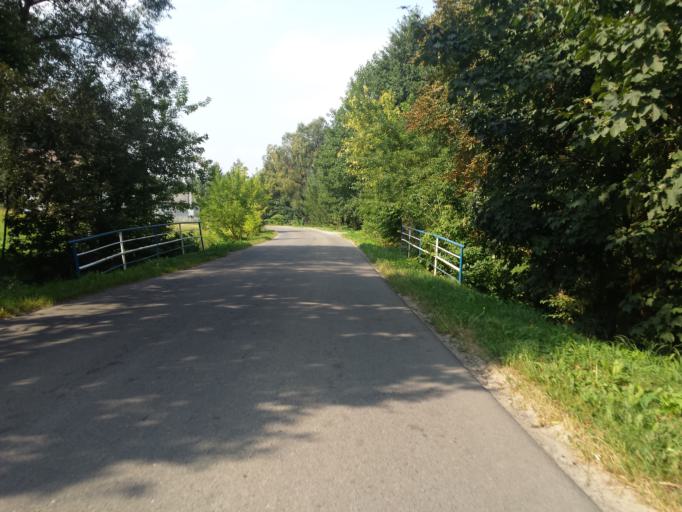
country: PL
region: Subcarpathian Voivodeship
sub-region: Powiat rzeszowski
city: Blazowa
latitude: 49.8511
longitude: 22.1393
